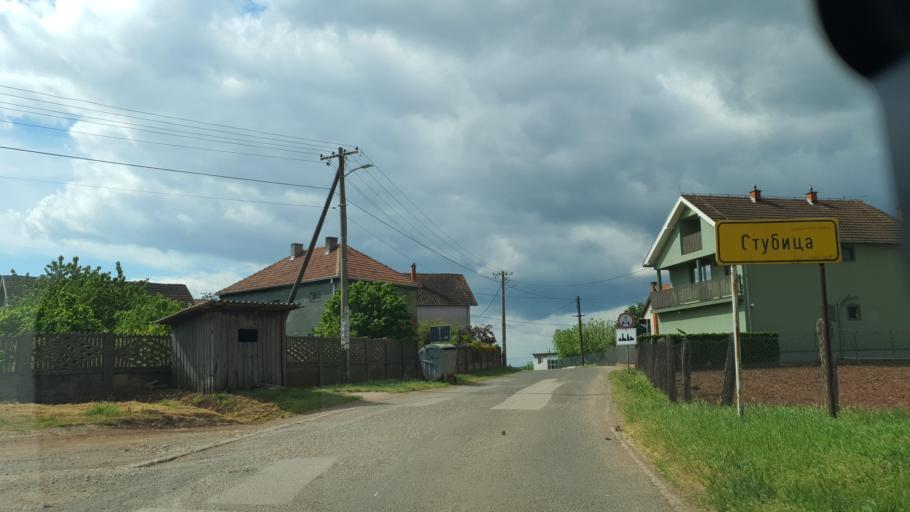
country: RS
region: Central Serbia
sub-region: Pomoravski Okrug
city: Paracin
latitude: 43.9469
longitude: 21.4928
